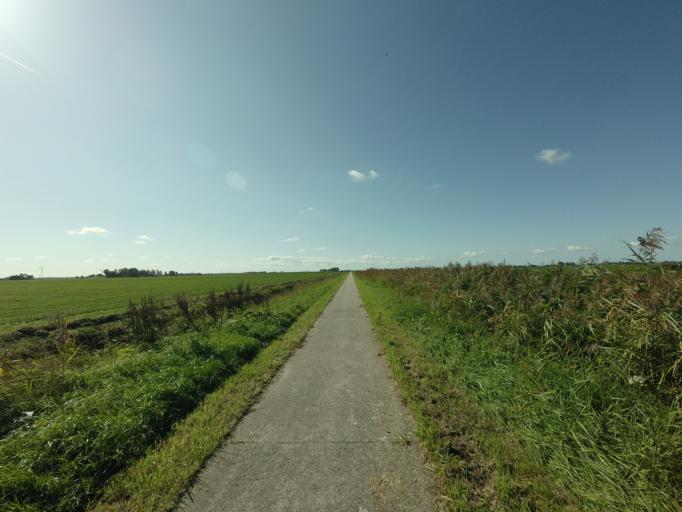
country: NL
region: Friesland
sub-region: Gemeente Boarnsterhim
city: Reduzum
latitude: 53.1379
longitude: 5.7610
